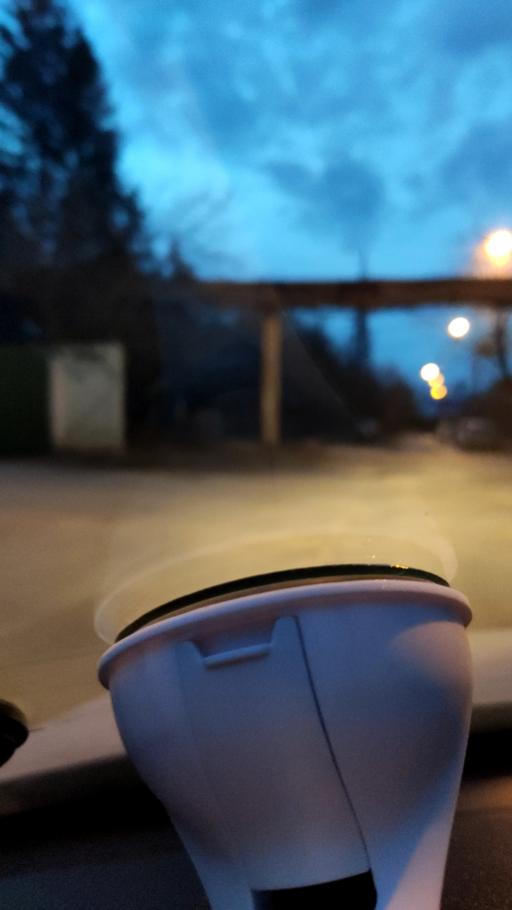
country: RU
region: Samara
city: Volzhskiy
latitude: 53.3514
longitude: 50.2086
